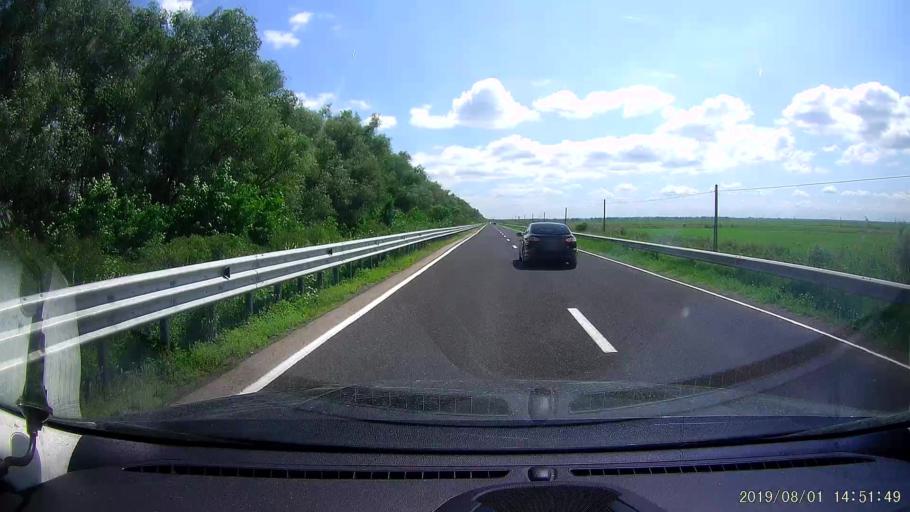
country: RO
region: Braila
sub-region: Comuna Vadeni
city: Vadeni
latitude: 45.3687
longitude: 28.0149
